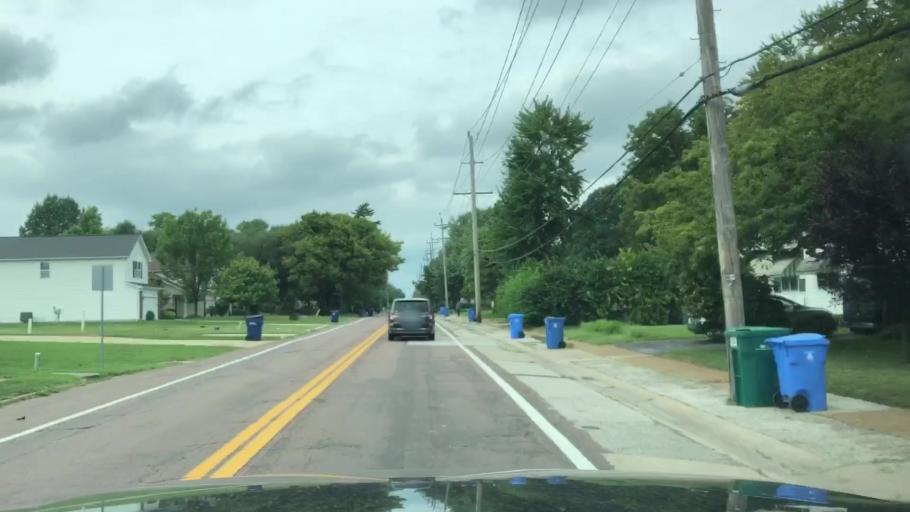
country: US
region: Missouri
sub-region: Saint Louis County
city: Florissant
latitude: 38.7983
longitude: -90.3413
